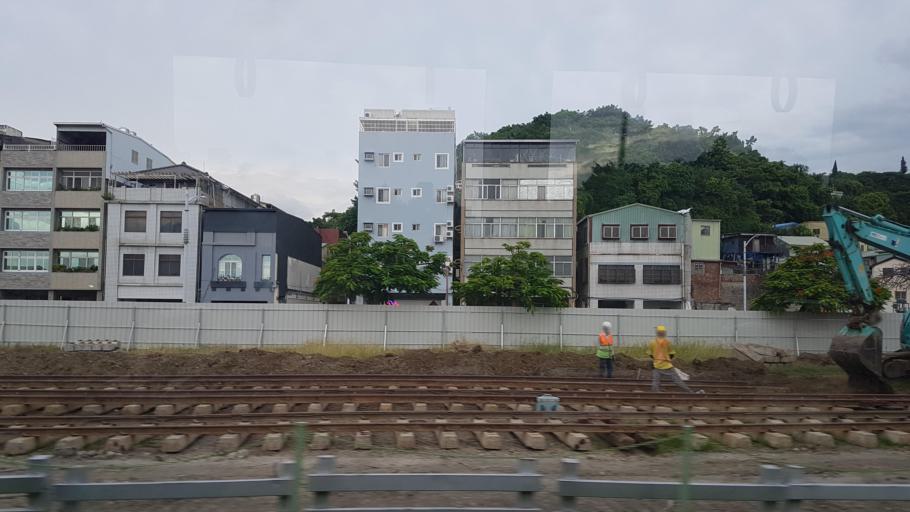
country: TW
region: Kaohsiung
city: Kaohsiung
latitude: 22.6234
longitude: 120.2767
